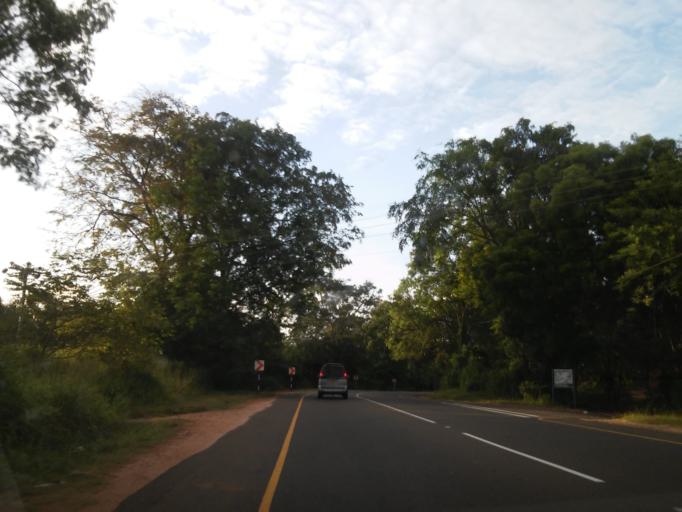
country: LK
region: North Central
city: Anuradhapura
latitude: 8.1798
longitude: 80.5298
